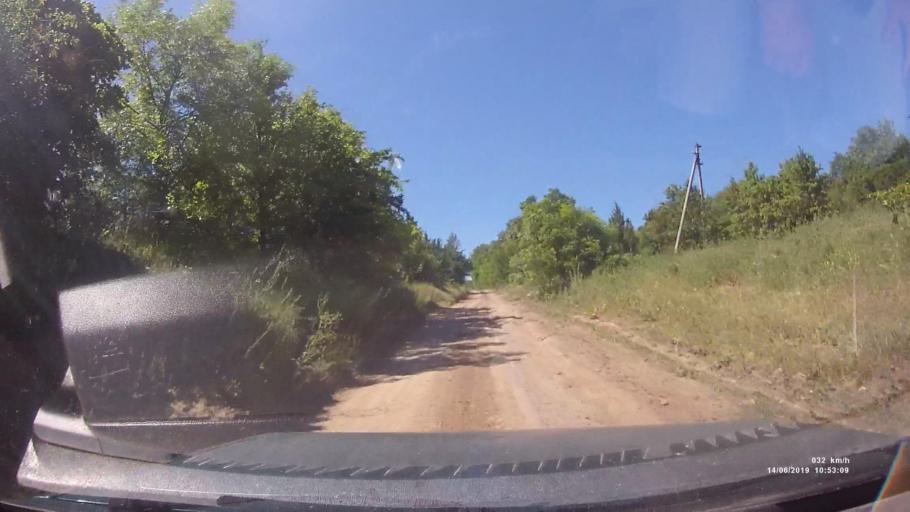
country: RU
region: Rostov
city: Kazanskaya
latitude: 49.8640
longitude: 41.3826
